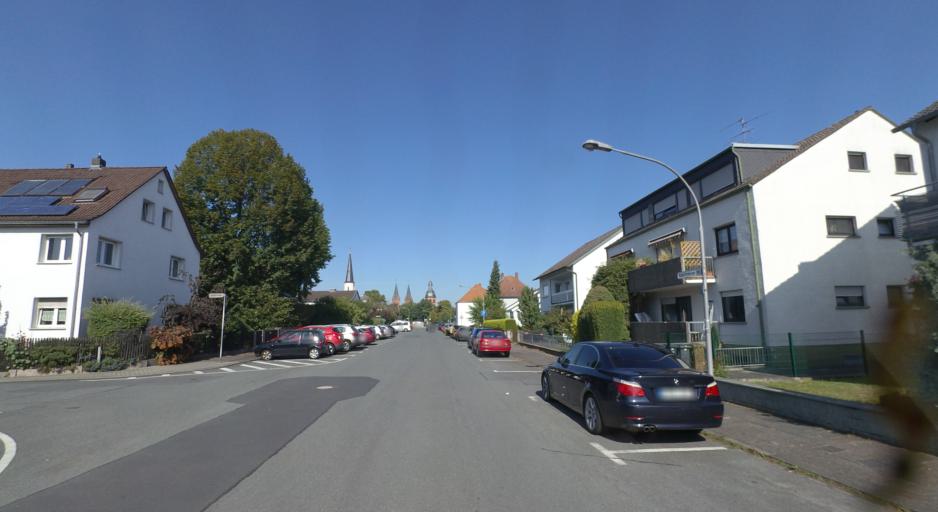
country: DE
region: Hesse
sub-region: Regierungsbezirk Darmstadt
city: Seligenstadt
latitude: 50.0401
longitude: 8.9830
